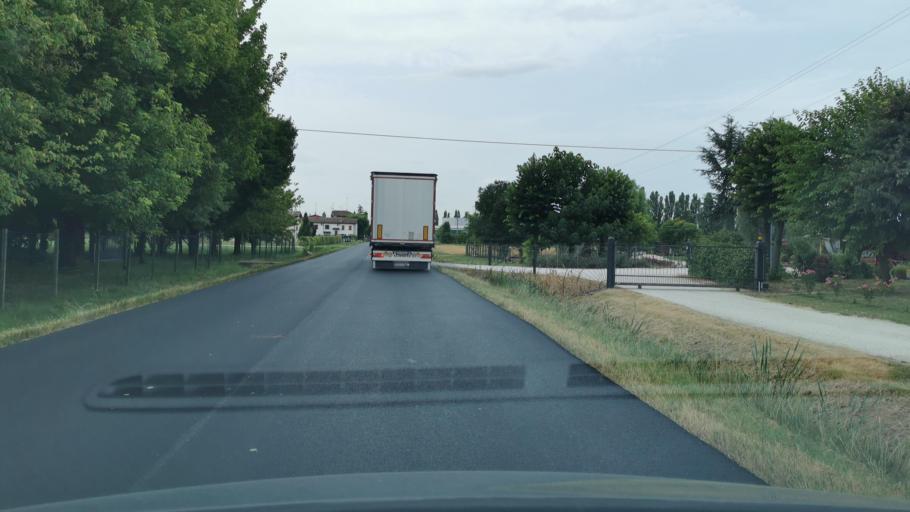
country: IT
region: Emilia-Romagna
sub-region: Provincia di Modena
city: Villanova
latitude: 44.7011
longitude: 10.8939
